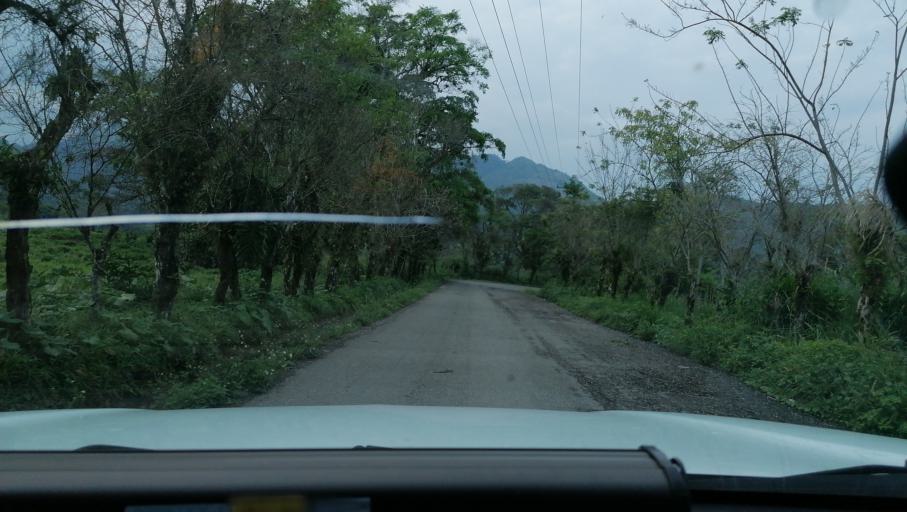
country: MX
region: Chiapas
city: Ixtacomitan
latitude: 17.3445
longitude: -93.1312
